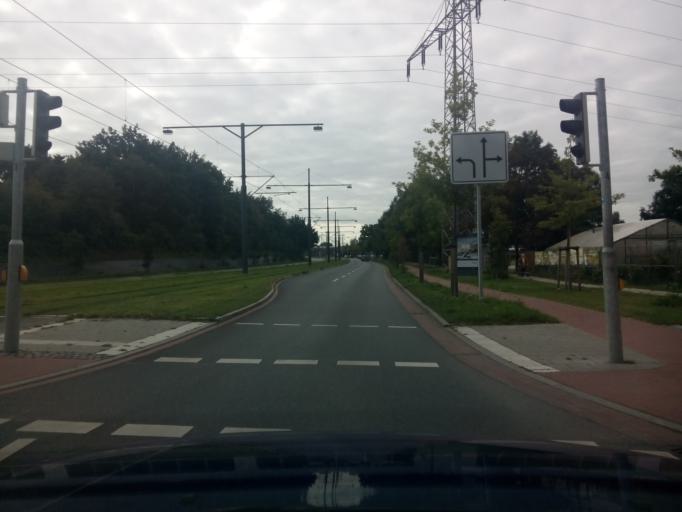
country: DE
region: Lower Saxony
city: Lilienthal
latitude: 53.1298
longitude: 8.8990
